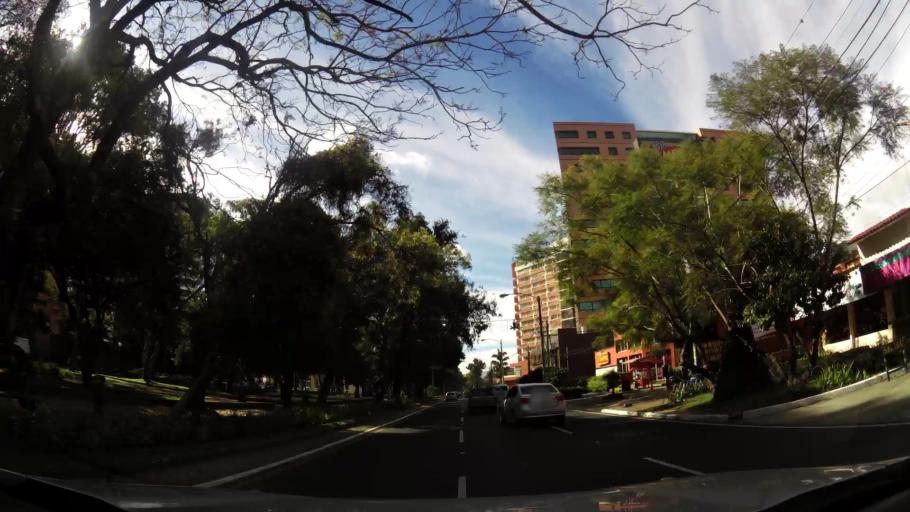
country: GT
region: Guatemala
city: Santa Catarina Pinula
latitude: 14.5885
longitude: -90.5202
